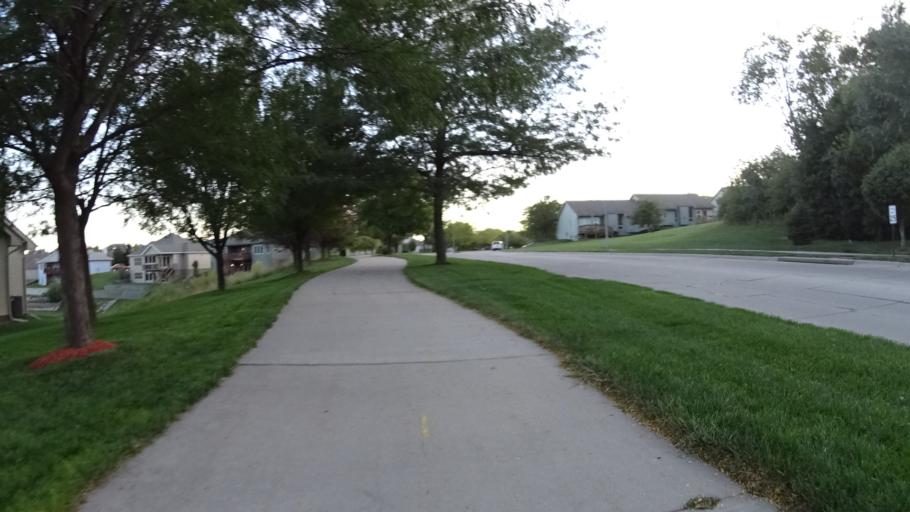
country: US
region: Nebraska
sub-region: Sarpy County
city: Papillion
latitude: 41.1372
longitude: -95.9867
